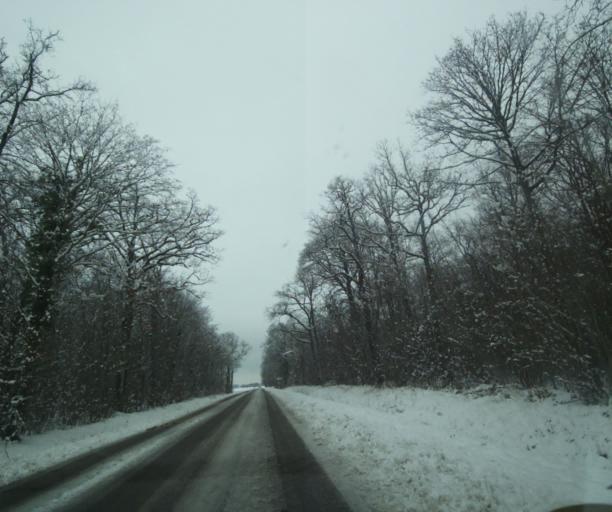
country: FR
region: Champagne-Ardenne
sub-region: Departement de la Haute-Marne
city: Montier-en-Der
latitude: 48.5280
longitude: 4.7489
